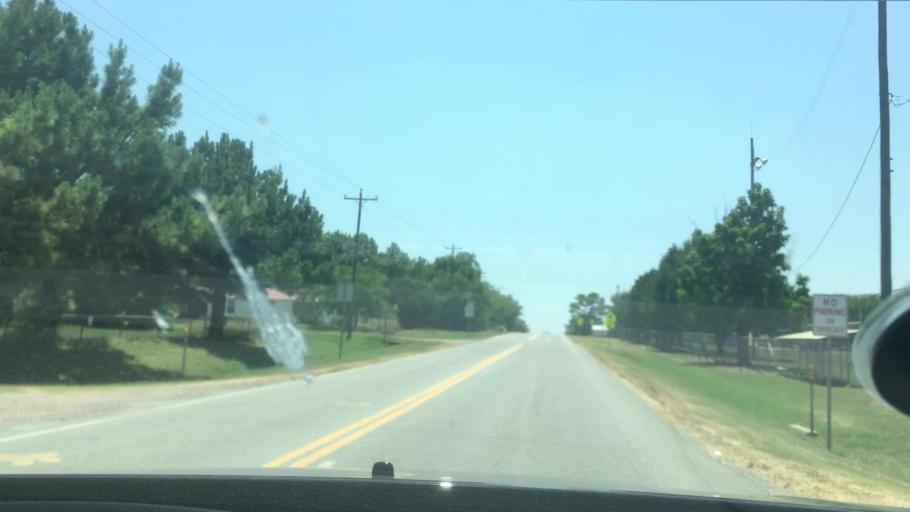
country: US
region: Oklahoma
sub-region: Coal County
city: Coalgate
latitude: 34.6043
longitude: -96.4245
